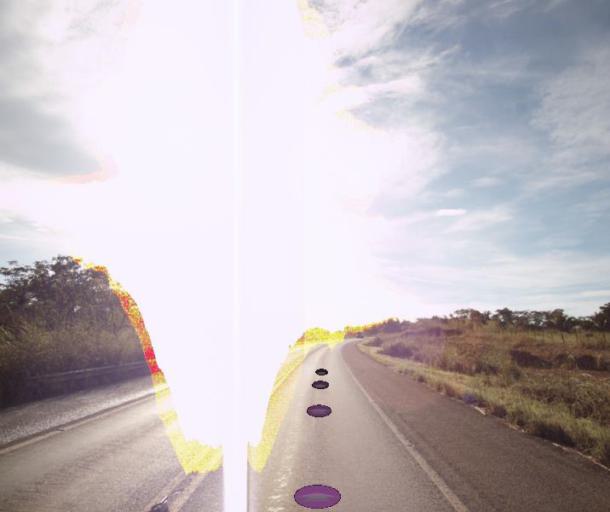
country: BR
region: Goias
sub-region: Pirenopolis
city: Pirenopolis
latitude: -15.7707
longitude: -48.5482
